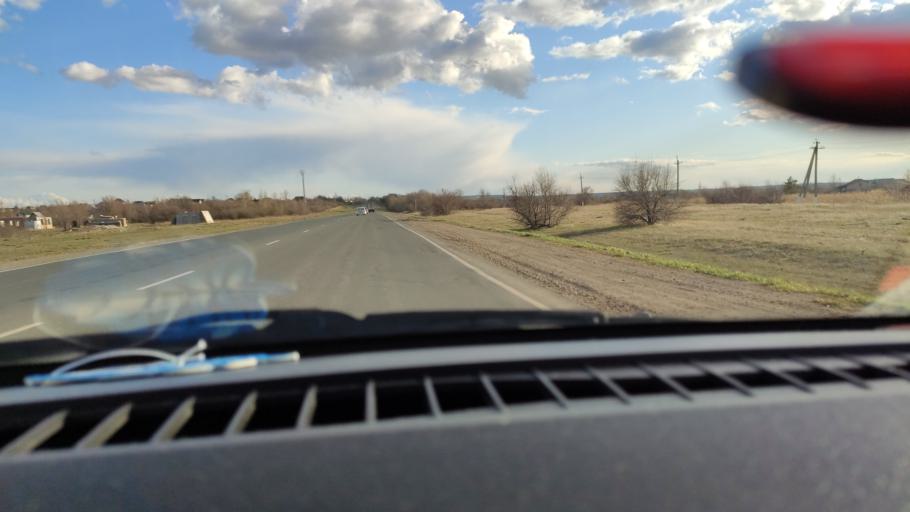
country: RU
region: Saratov
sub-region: Saratovskiy Rayon
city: Saratov
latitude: 51.6865
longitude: 46.0038
